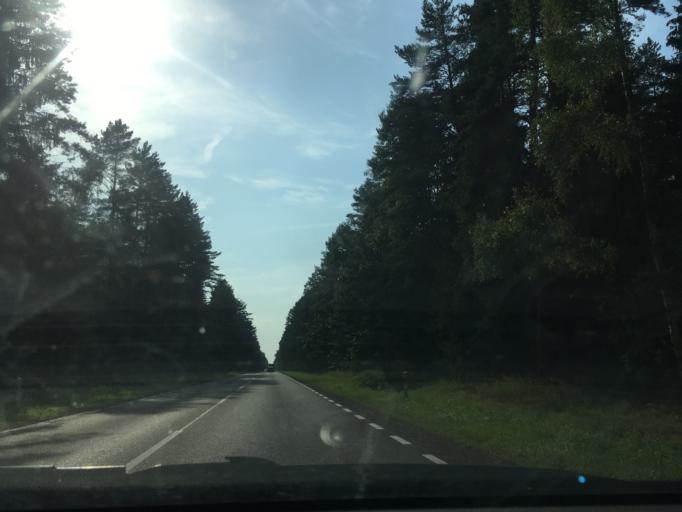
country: PL
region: Podlasie
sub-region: Powiat bialostocki
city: Suprasl
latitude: 53.1256
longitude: 23.3985
